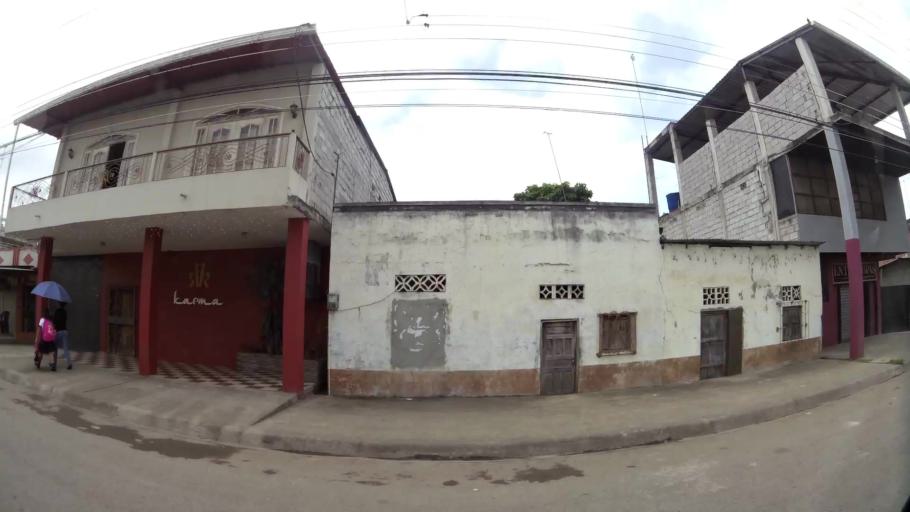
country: EC
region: El Oro
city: Pasaje
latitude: -3.2419
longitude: -79.8286
